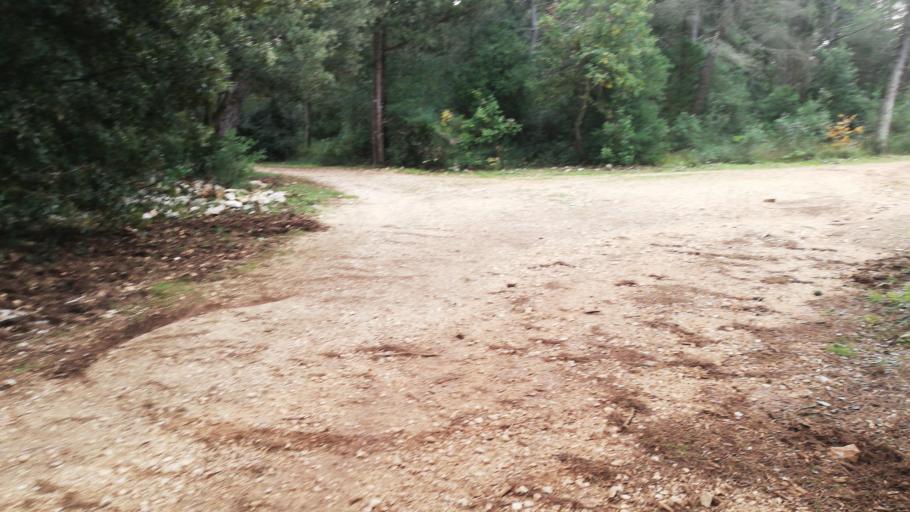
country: IT
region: Apulia
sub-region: Provincia di Bari
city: Cassano delle Murge
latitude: 40.8792
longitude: 16.7129
